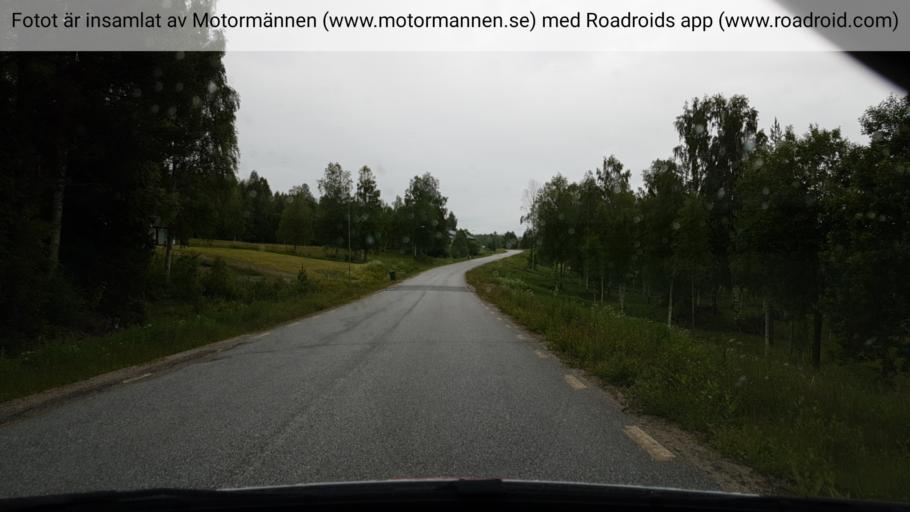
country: SE
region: Vaesterbotten
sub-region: Bjurholms Kommun
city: Bjurholm
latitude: 64.0259
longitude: 19.3395
